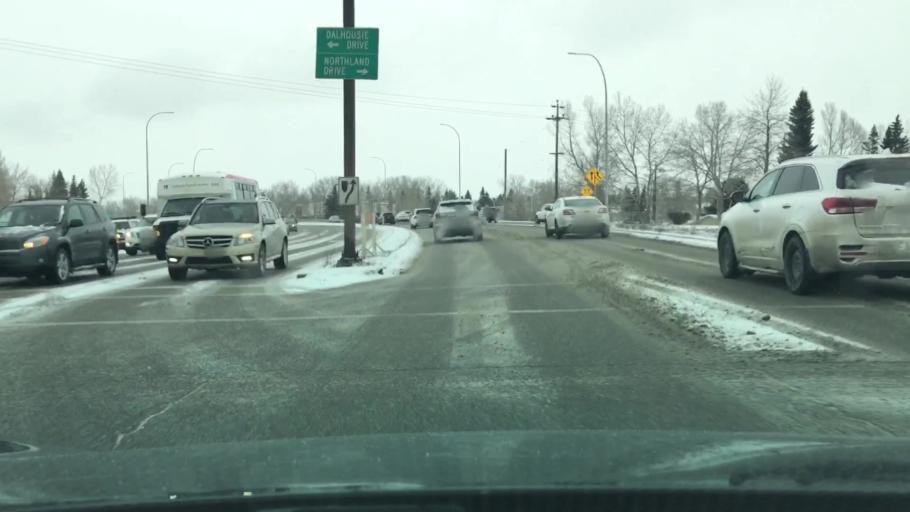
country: CA
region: Alberta
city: Calgary
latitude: 51.1032
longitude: -114.1442
